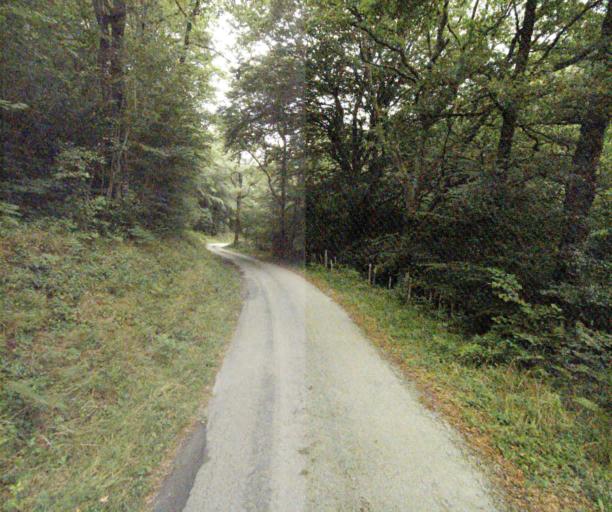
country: FR
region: Midi-Pyrenees
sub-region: Departement du Tarn
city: Soreze
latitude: 43.4277
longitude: 2.0908
